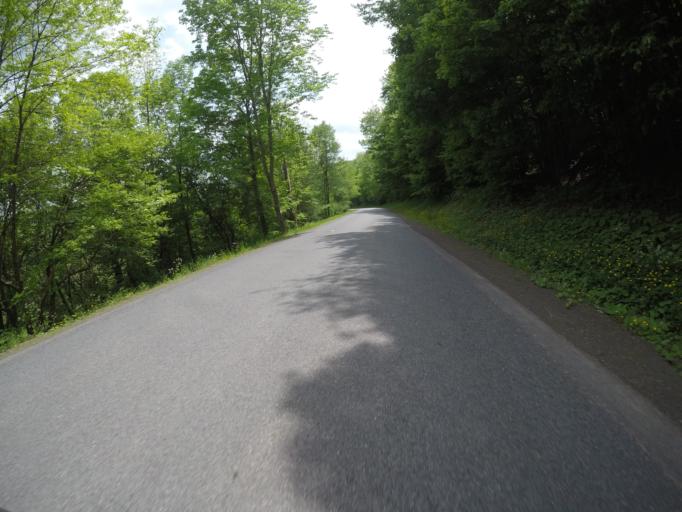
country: US
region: New York
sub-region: Delaware County
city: Stamford
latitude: 42.2299
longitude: -74.6928
